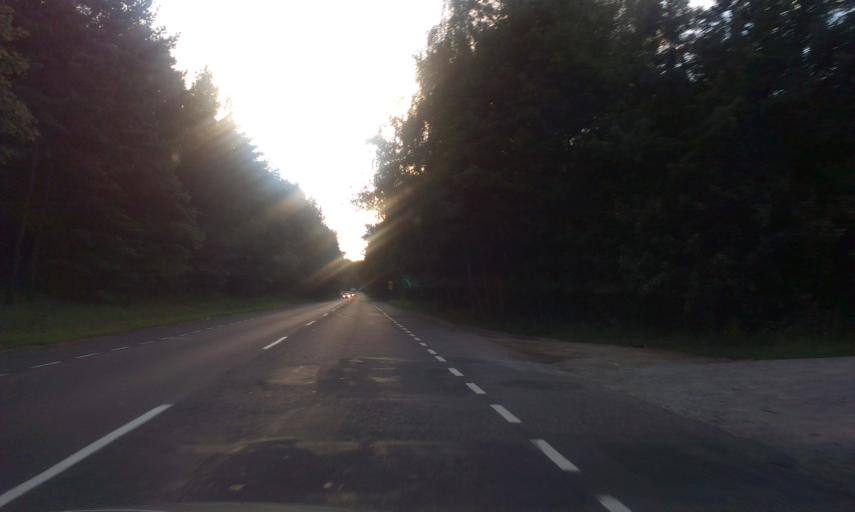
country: PL
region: West Pomeranian Voivodeship
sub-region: Powiat koszalinski
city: Sianow
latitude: 54.2227
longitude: 16.2522
